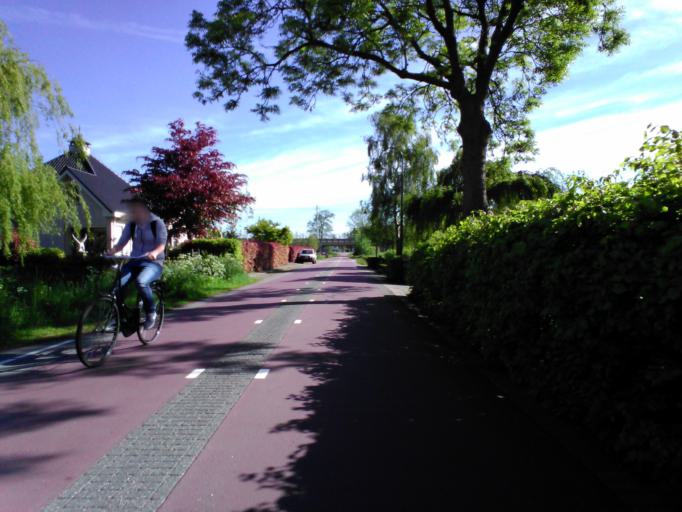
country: NL
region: South Holland
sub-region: Gemeente Rijnwoude
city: Benthuizen
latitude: 52.0673
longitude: 4.5268
